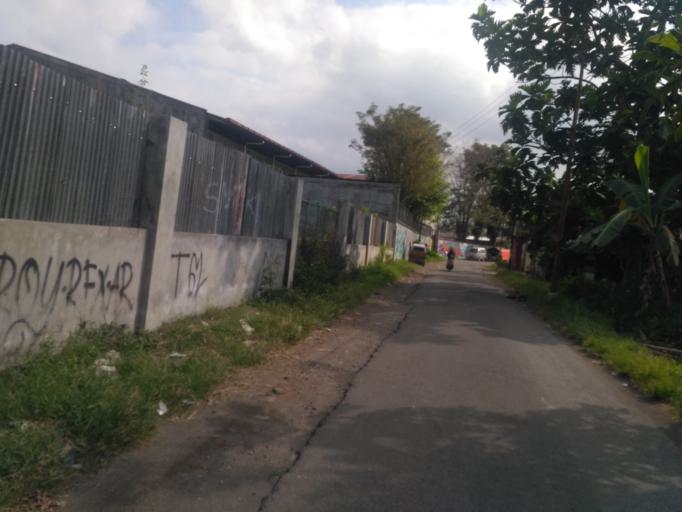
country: ID
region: Daerah Istimewa Yogyakarta
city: Yogyakarta
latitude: -7.7634
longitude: 110.3586
